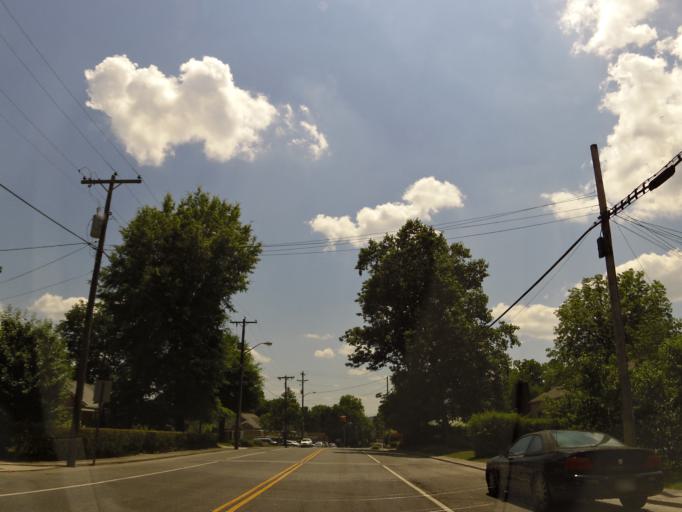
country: US
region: Tennessee
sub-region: Rhea County
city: Dayton
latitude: 35.4983
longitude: -85.0096
